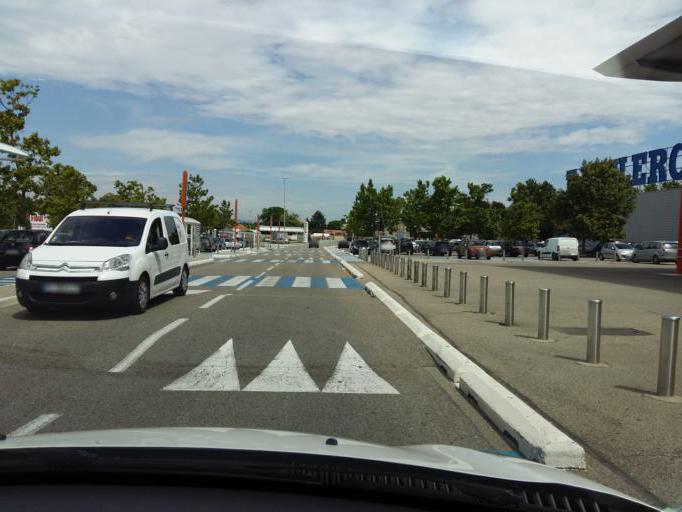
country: FR
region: Rhone-Alpes
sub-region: Departement de la Drome
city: Saint-Paul-Trois-Chateaux
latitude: 44.3209
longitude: 4.7439
